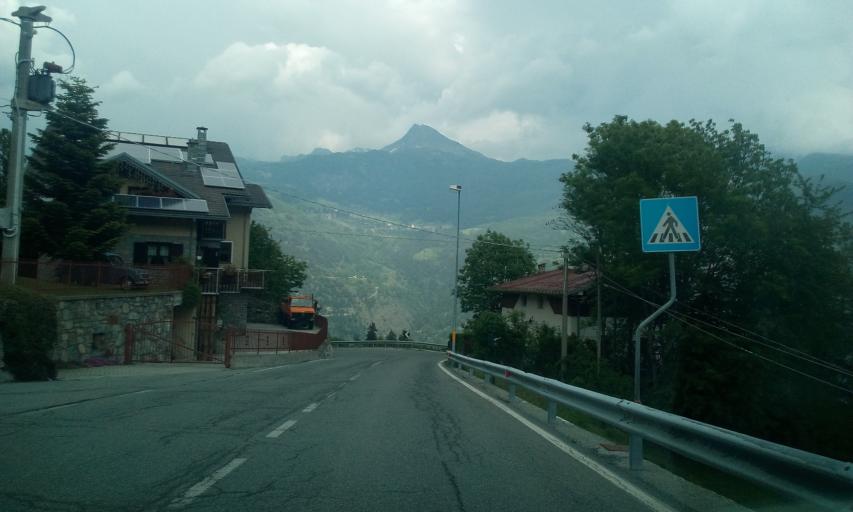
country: IT
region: Aosta Valley
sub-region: Valle d'Aosta
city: Mongnod
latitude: 45.7974
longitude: 7.5719
